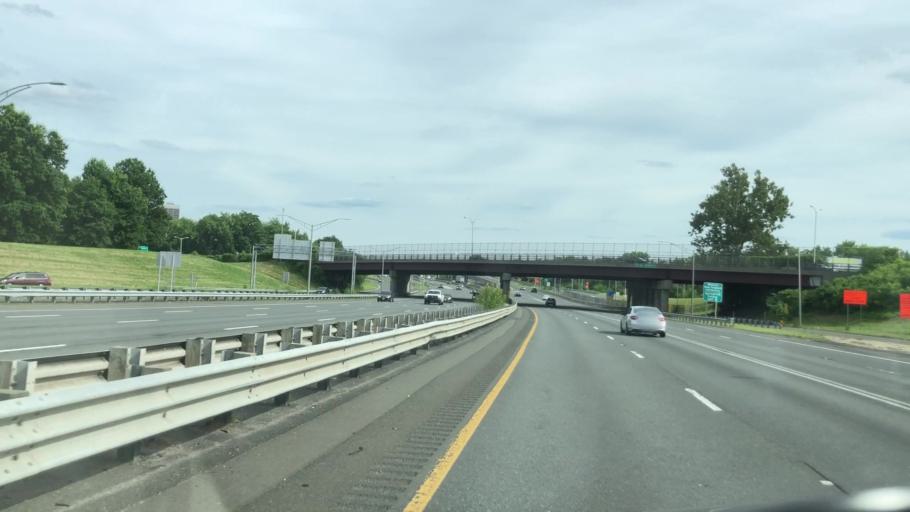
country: US
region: Massachusetts
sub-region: Hampden County
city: West Springfield
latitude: 42.1127
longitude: -72.6073
